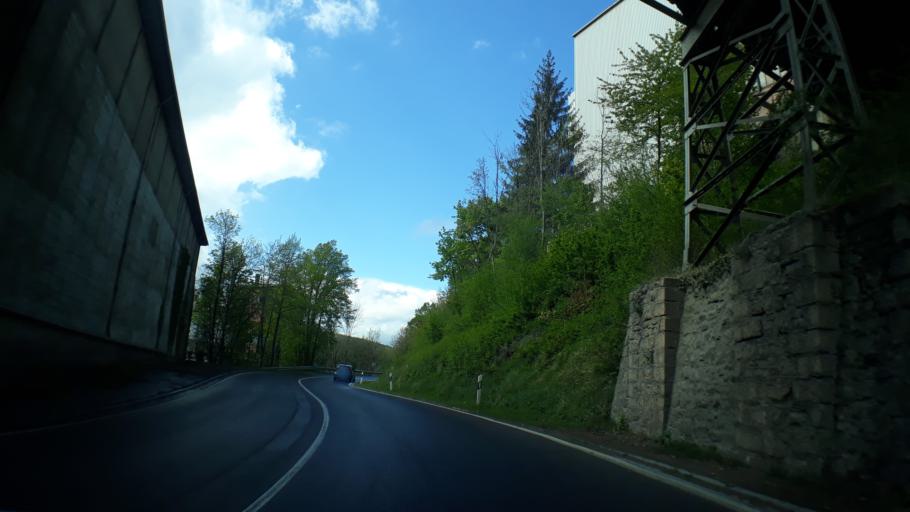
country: DE
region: North Rhine-Westphalia
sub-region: Regierungsbezirk Koln
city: Kall
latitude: 50.5207
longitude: 6.5592
